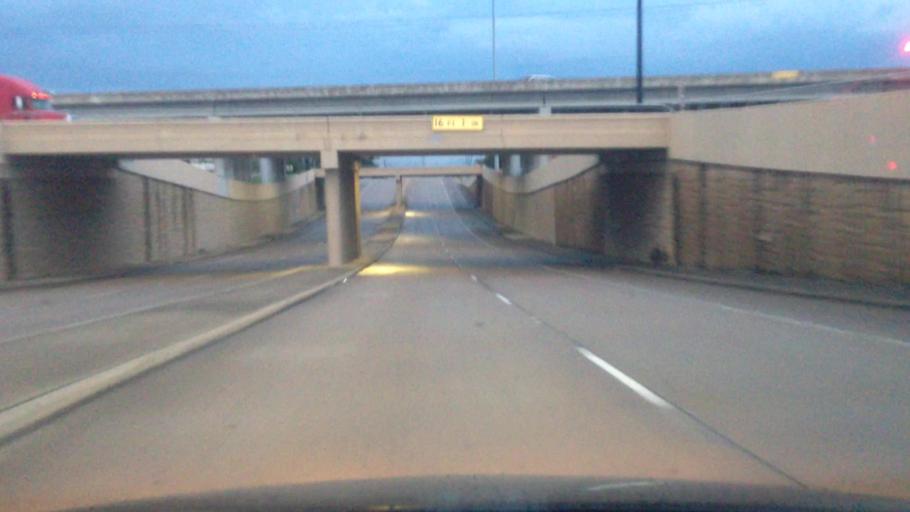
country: US
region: Texas
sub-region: Tarrant County
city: Arlington
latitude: 32.7357
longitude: -97.0636
